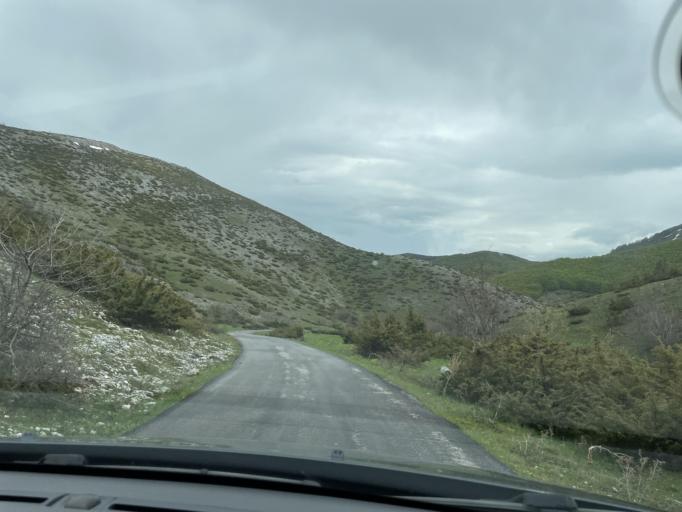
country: MK
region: Opstina Rostusa
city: Rostusha
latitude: 41.6080
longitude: 20.6816
